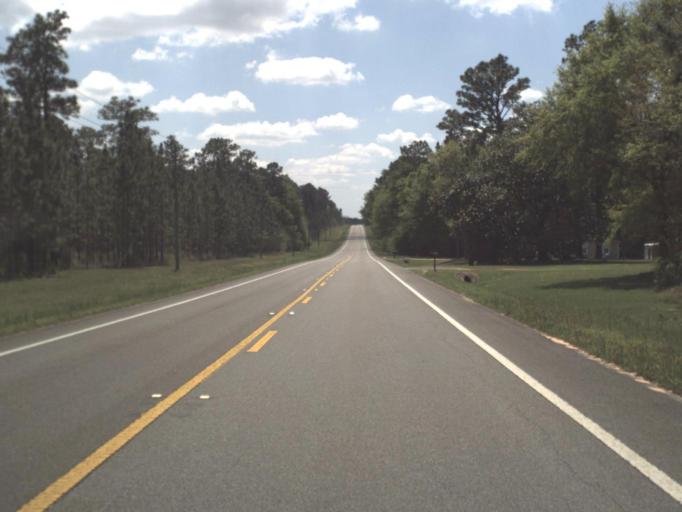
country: US
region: Florida
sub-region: Okaloosa County
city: Crestview
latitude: 30.8831
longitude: -86.6638
